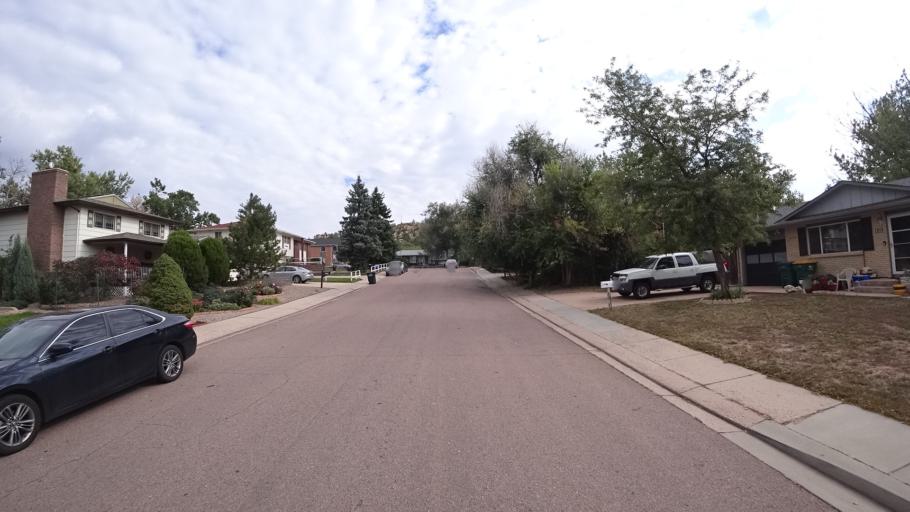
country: US
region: Colorado
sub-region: El Paso County
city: Cimarron Hills
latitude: 38.8566
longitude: -104.7455
